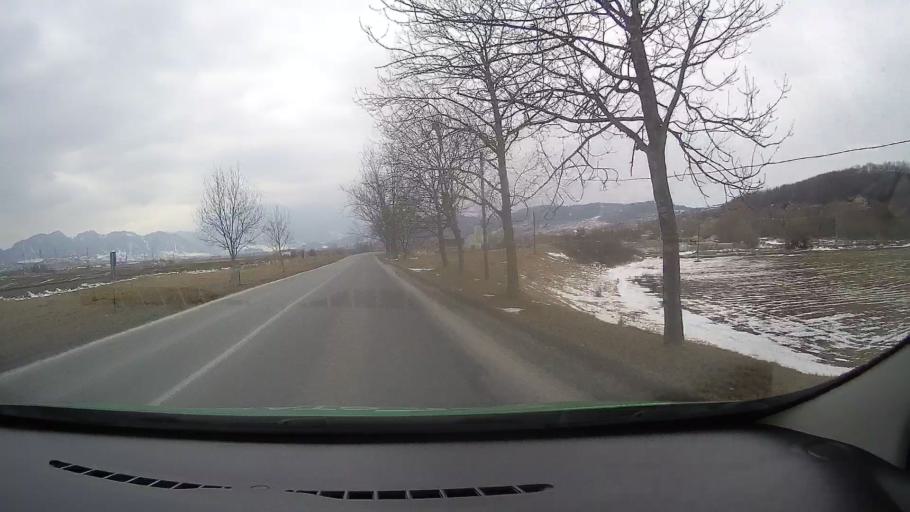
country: RO
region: Brasov
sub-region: Comuna Zarnesti
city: Tohanu Nou
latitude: 45.5770
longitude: 25.3979
